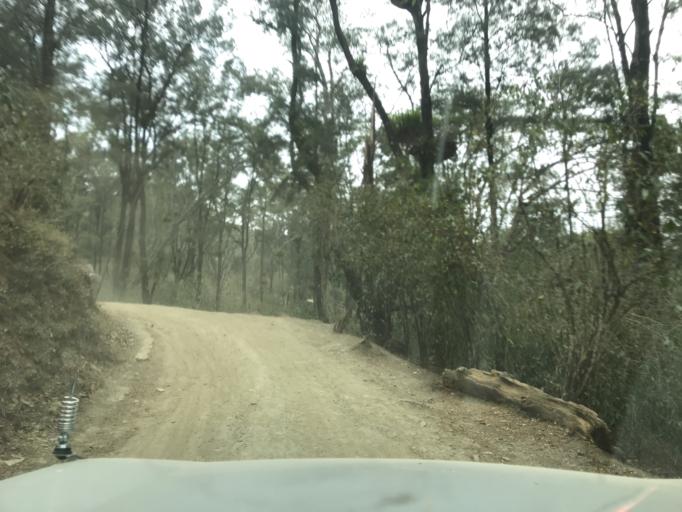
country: TL
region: Ermera
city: Gleno
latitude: -8.8347
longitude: 125.4498
